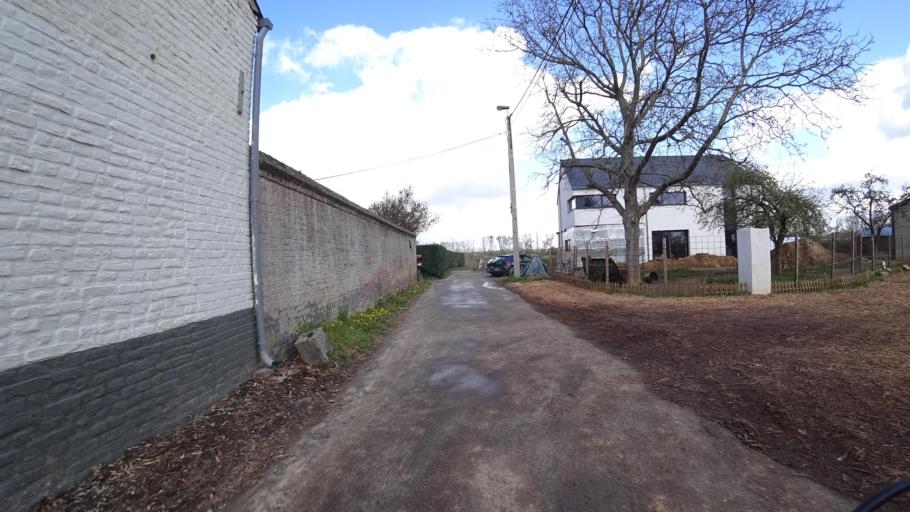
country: BE
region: Wallonia
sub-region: Province du Brabant Wallon
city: Walhain-Saint-Paul
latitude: 50.6466
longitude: 4.7074
